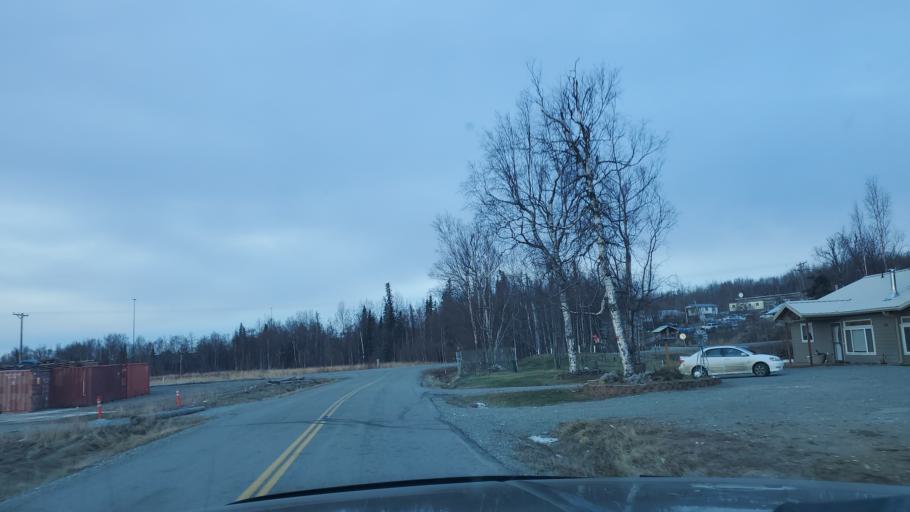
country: US
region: Alaska
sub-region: Matanuska-Susitna Borough
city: Lakes
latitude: 61.5729
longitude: -149.3432
